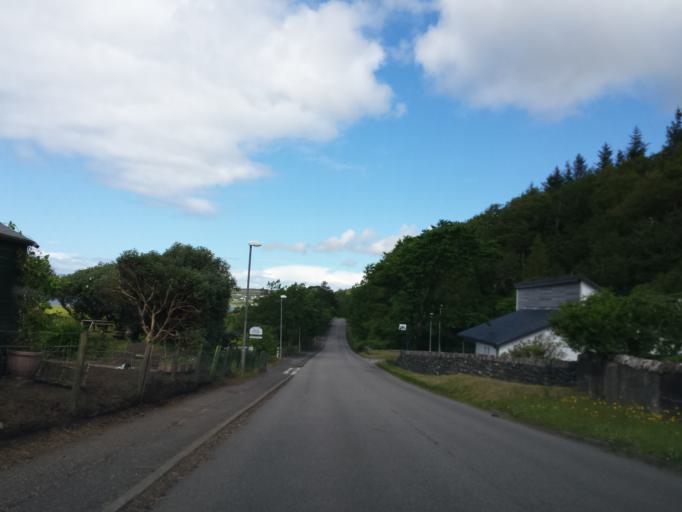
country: GB
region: Scotland
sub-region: Highland
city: Ullapool
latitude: 57.7141
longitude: -5.6808
